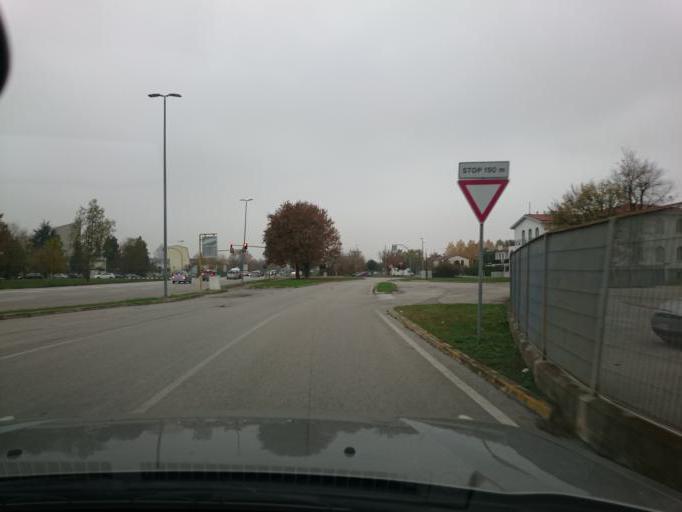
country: IT
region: Veneto
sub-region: Provincia di Padova
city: Legnaro
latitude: 45.3533
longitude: 11.9528
